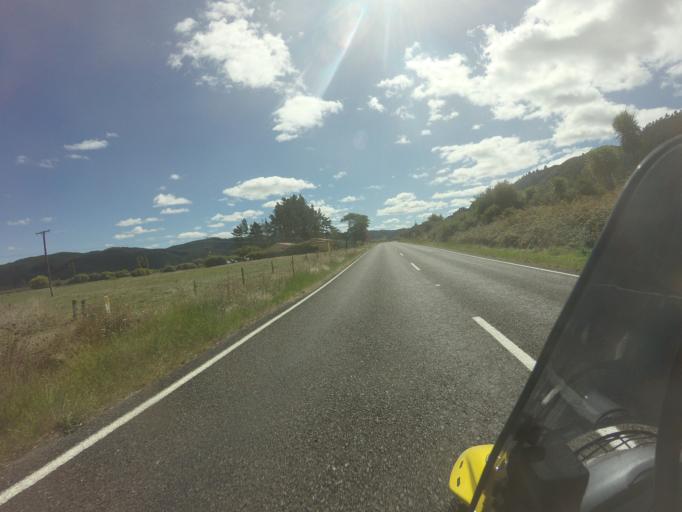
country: NZ
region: Bay of Plenty
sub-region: Kawerau District
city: Kawerau
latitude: -38.1989
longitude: 176.8429
